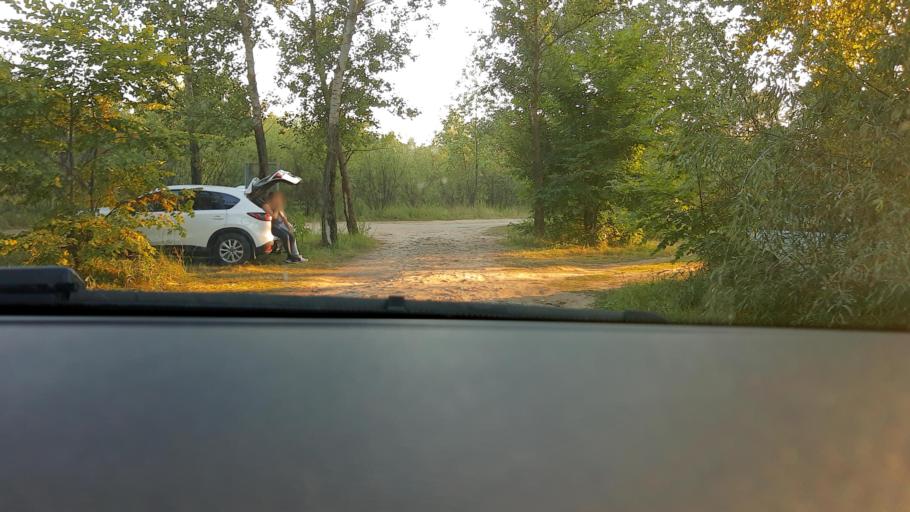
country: RU
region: Nizjnij Novgorod
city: Bor
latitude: 56.3292
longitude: 44.0521
